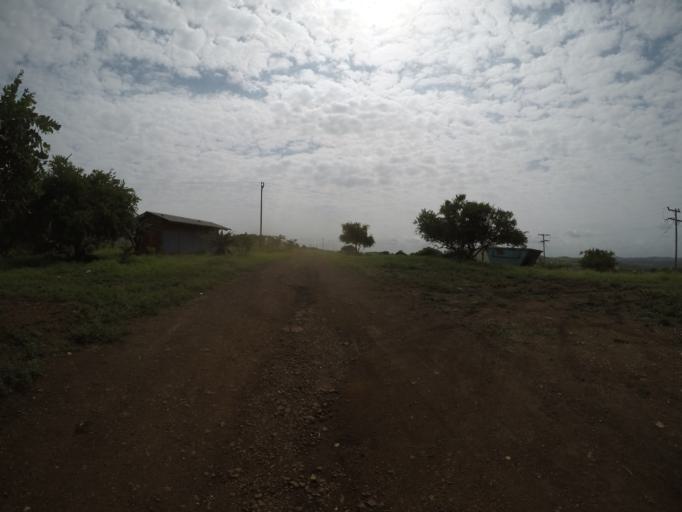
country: ZA
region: KwaZulu-Natal
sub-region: uThungulu District Municipality
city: Empangeni
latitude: -28.6205
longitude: 31.9047
